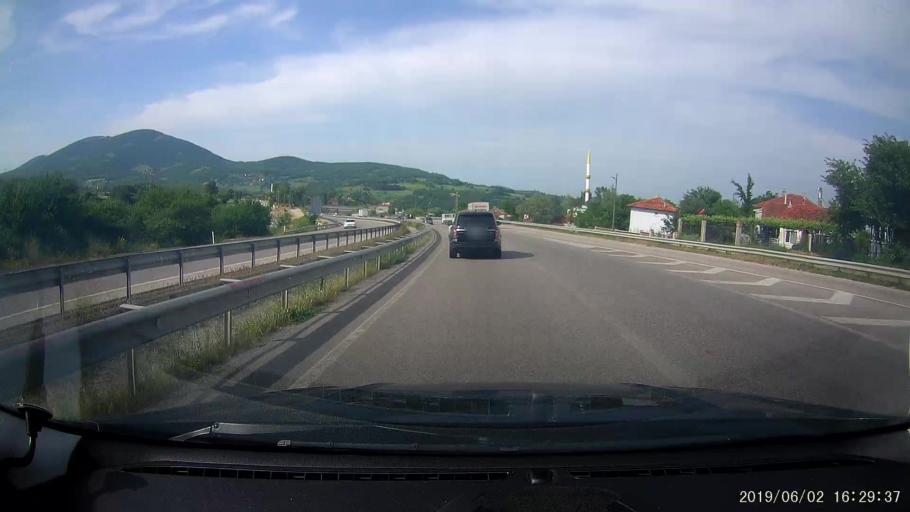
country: TR
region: Samsun
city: Ladik
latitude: 41.0149
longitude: 35.8715
